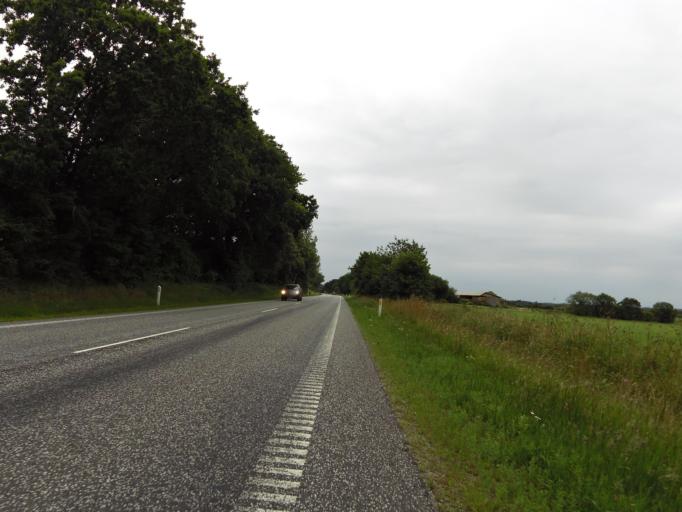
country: DK
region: South Denmark
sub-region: Tonder Kommune
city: Logumkloster
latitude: 55.0992
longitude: 8.9408
